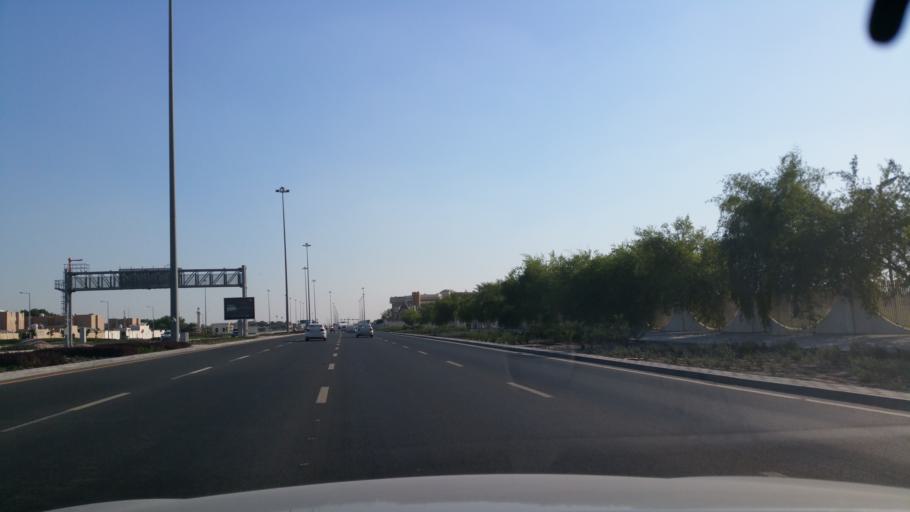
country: QA
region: Baladiyat ar Rayyan
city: Ar Rayyan
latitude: 25.2755
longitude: 51.4311
